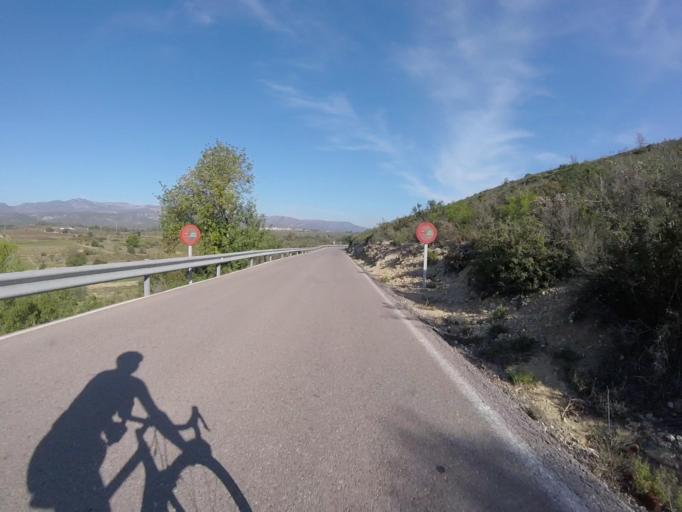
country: ES
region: Valencia
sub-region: Provincia de Castello
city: Benlloch
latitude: 40.2478
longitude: 0.0766
